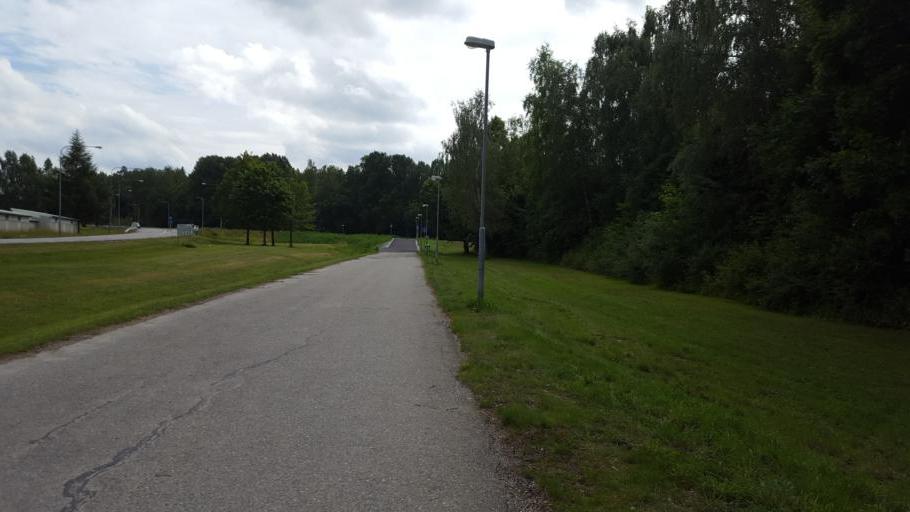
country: SE
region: Stockholm
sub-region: Upplands Vasby Kommun
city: Upplands Vaesby
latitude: 59.5082
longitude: 17.9007
